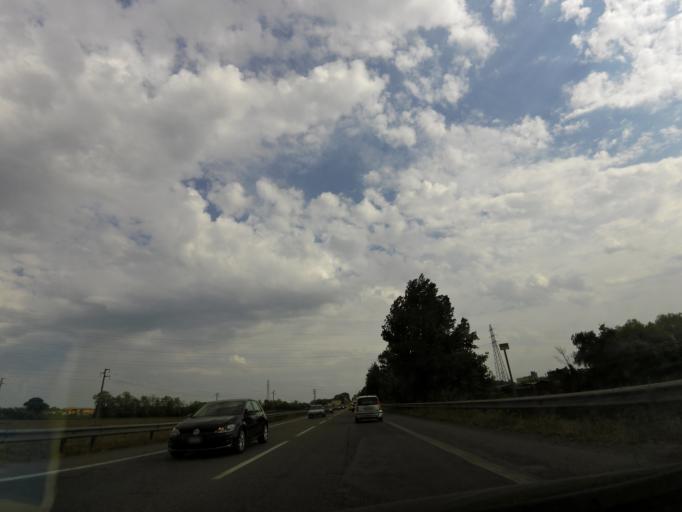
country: IT
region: Lombardy
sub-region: Citta metropolitana di Milano
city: Melegnano
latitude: 45.3717
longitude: 9.3116
